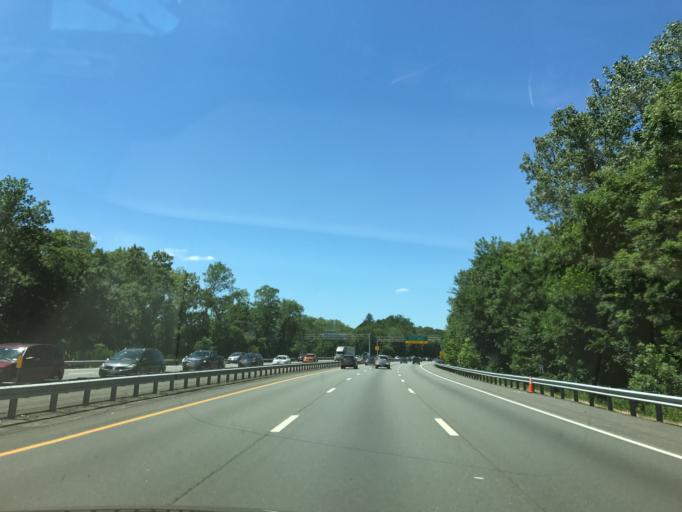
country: US
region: New York
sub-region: Rockland County
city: Spring Valley
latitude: 41.0969
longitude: -74.0448
